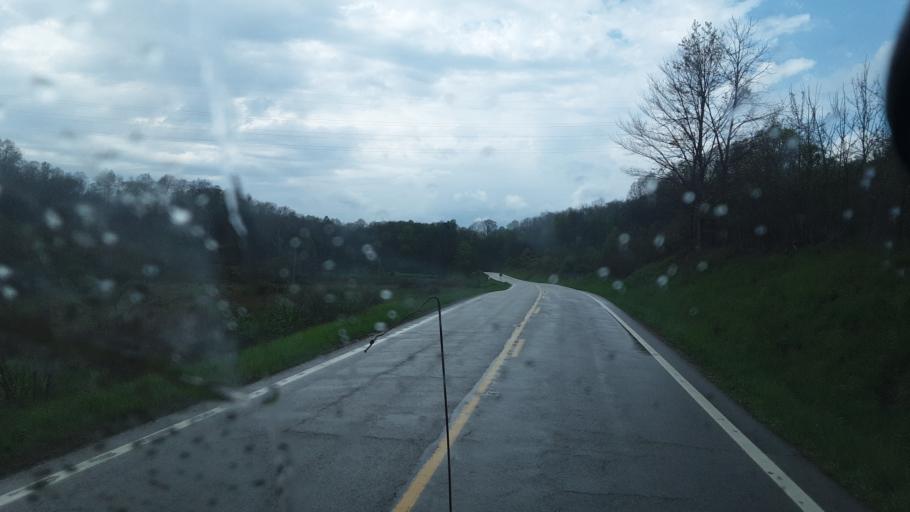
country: US
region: Ohio
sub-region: Guernsey County
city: Mantua
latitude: 40.0650
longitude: -81.7464
